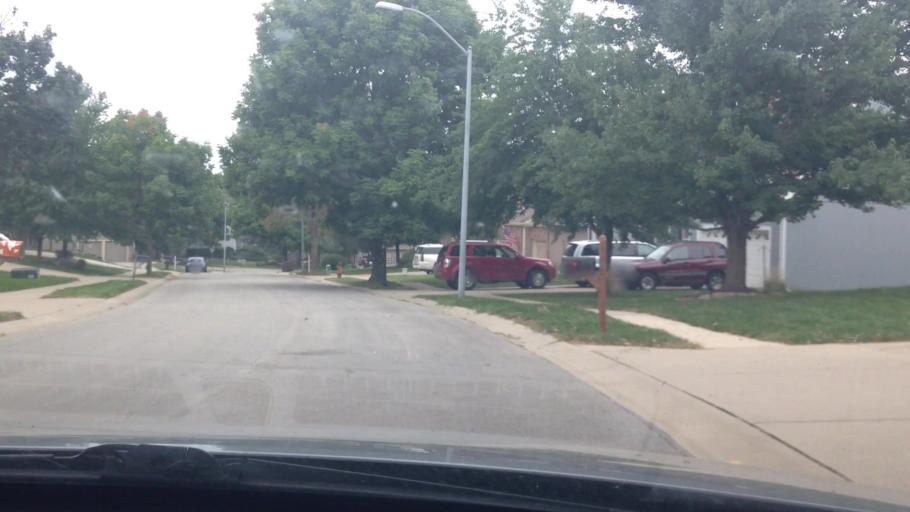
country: US
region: Missouri
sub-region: Platte County
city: Weatherby Lake
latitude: 39.2369
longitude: -94.6511
